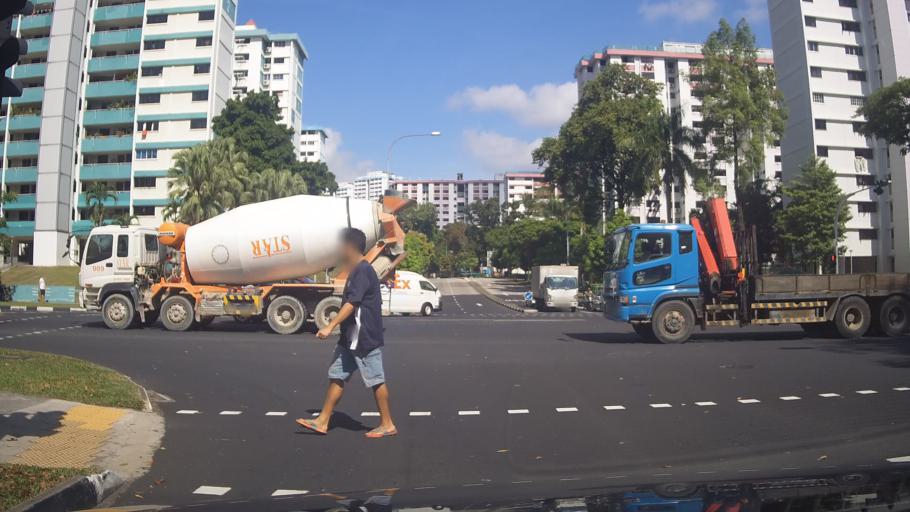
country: MY
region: Johor
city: Johor Bahru
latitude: 1.4417
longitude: 103.7755
